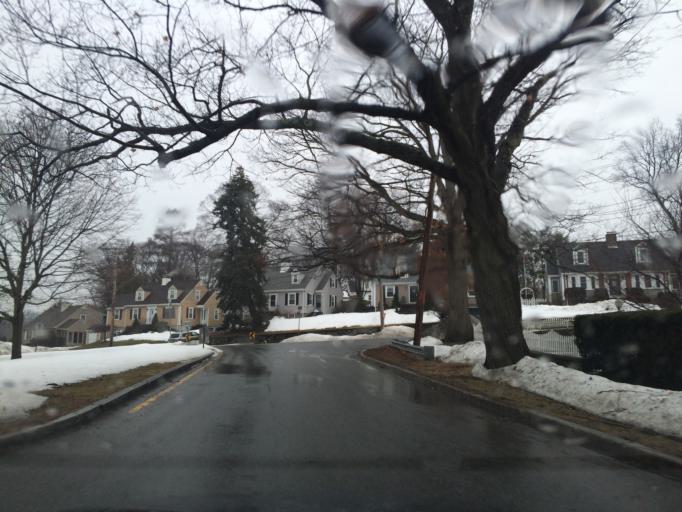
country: US
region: Massachusetts
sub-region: Middlesex County
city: Waltham
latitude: 42.3813
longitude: -71.2181
